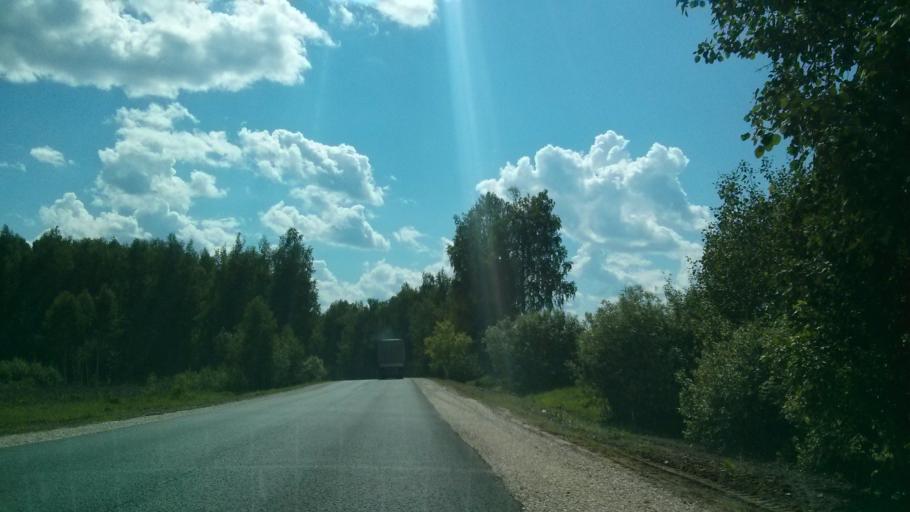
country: RU
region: Vladimir
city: Murom
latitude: 55.4986
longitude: 41.9060
